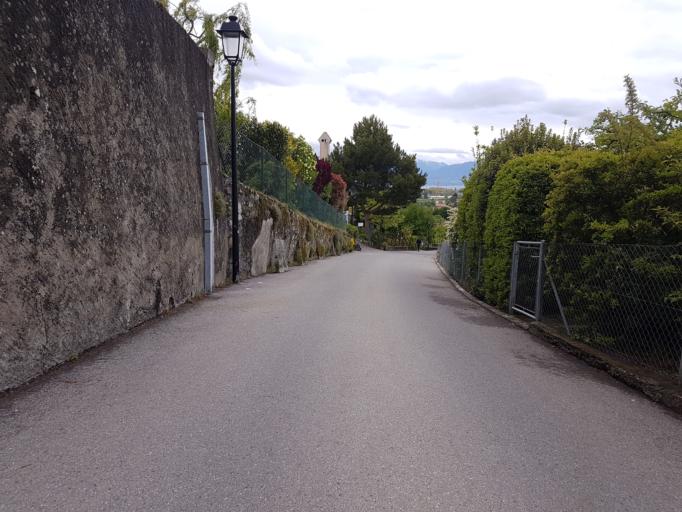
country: CH
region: Vaud
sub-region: Ouest Lausannois District
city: Ecublens
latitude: 46.5326
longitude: 6.5422
